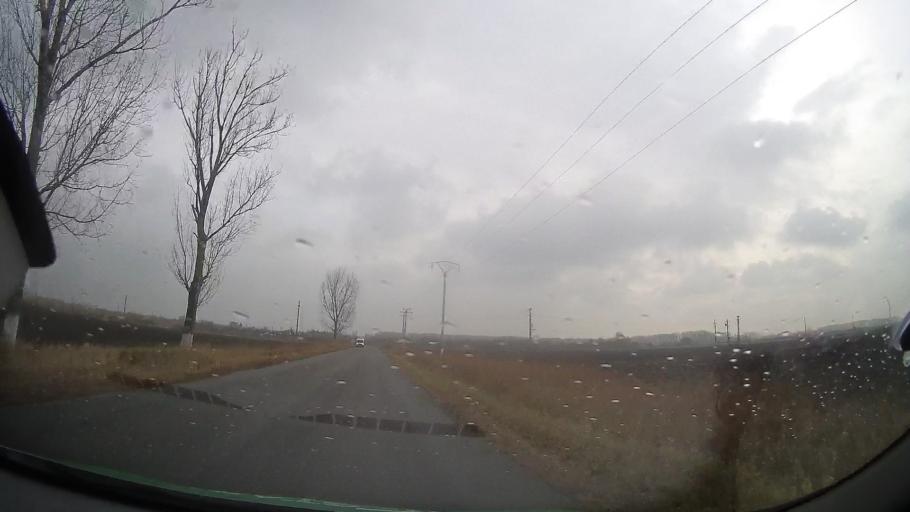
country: RO
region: Prahova
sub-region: Comuna Draganesti
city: Draganesti
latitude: 44.8314
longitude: 26.2746
